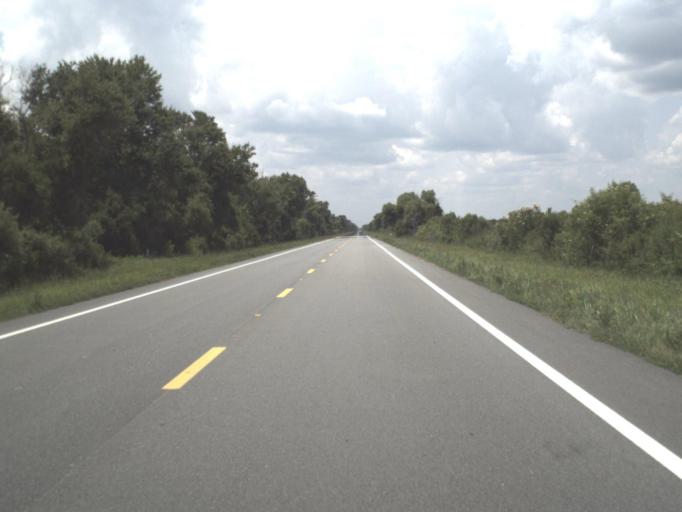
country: US
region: Florida
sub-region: Hamilton County
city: Jasper
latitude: 30.4408
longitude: -82.8766
